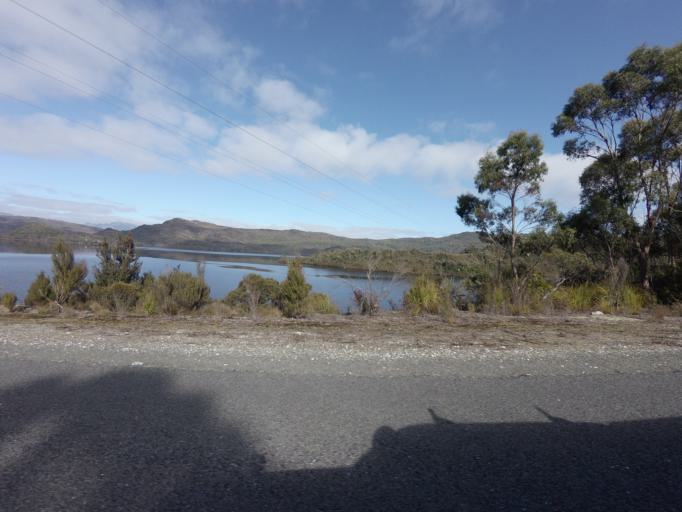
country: AU
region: Tasmania
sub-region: Huon Valley
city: Geeveston
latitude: -42.8284
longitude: 146.1261
